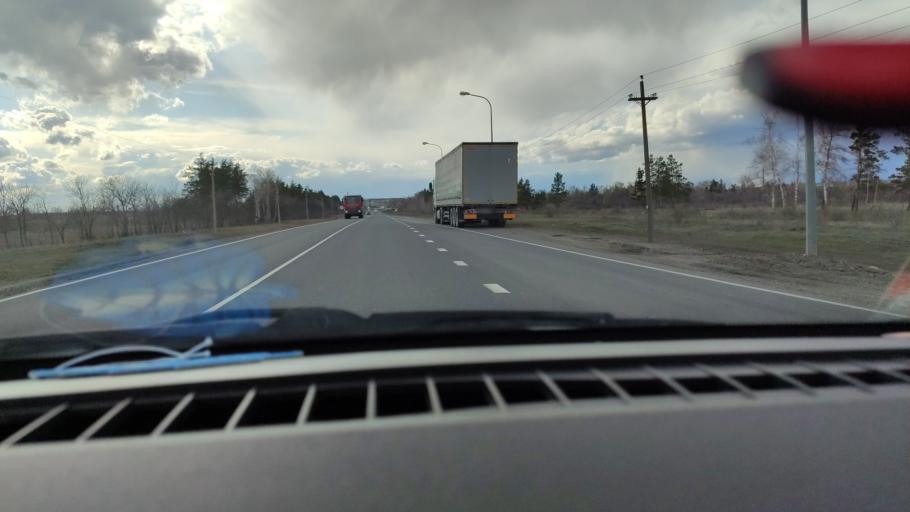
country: RU
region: Saratov
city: Sennoy
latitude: 52.1516
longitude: 46.9692
